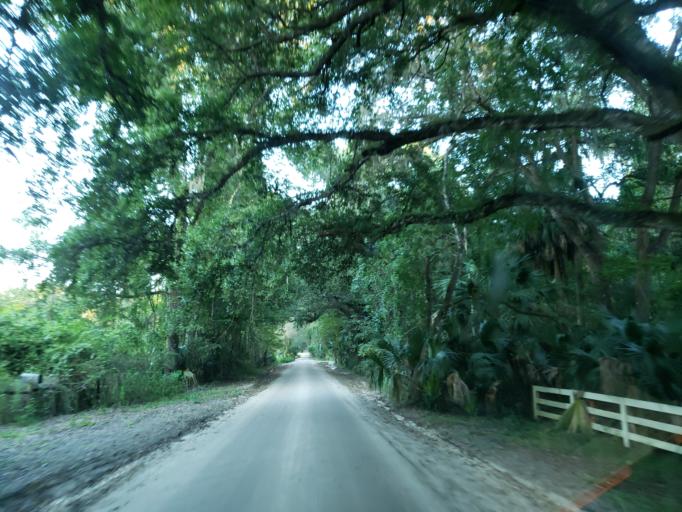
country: US
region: Florida
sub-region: Marion County
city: Citra
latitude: 29.4842
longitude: -82.2600
